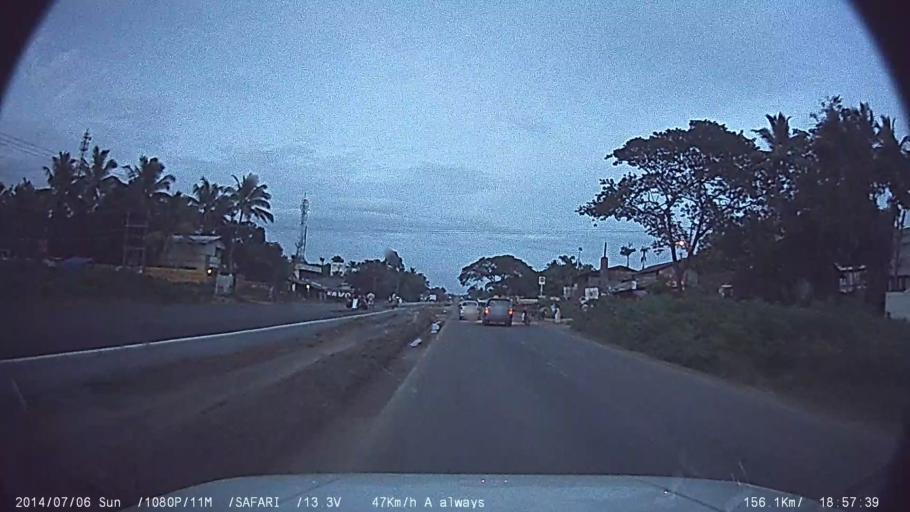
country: IN
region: Kerala
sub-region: Palakkad district
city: Palakkad
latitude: 10.7380
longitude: 76.6344
